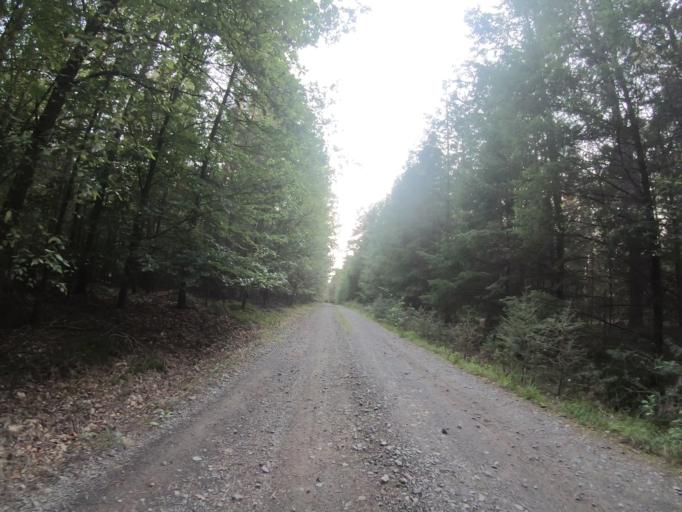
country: DE
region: Lower Saxony
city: Leiferde
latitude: 52.4690
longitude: 10.4522
